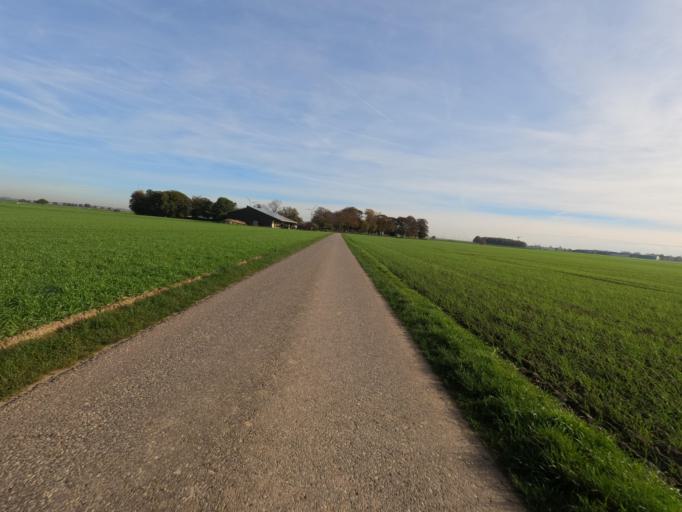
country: DE
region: North Rhine-Westphalia
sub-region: Regierungsbezirk Koln
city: Titz
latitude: 51.0602
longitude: 6.3888
